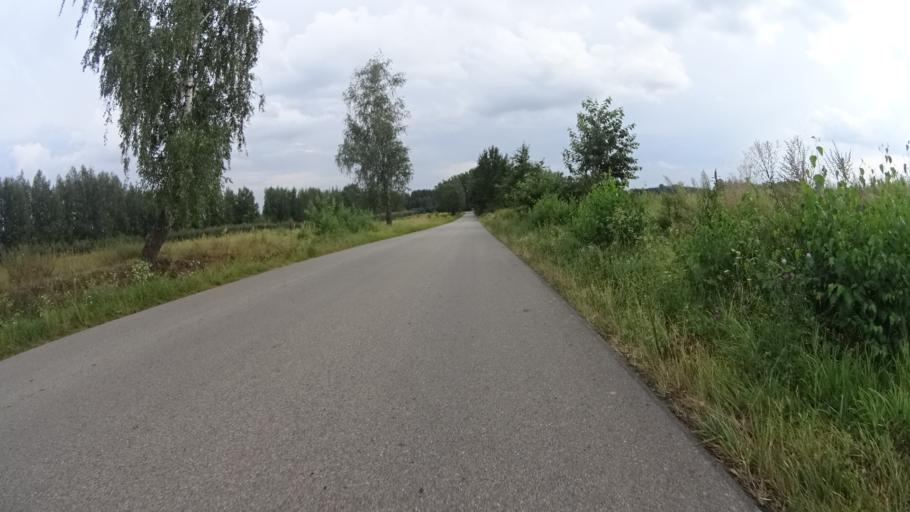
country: PL
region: Masovian Voivodeship
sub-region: Powiat grojecki
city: Goszczyn
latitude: 51.6922
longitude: 20.8572
